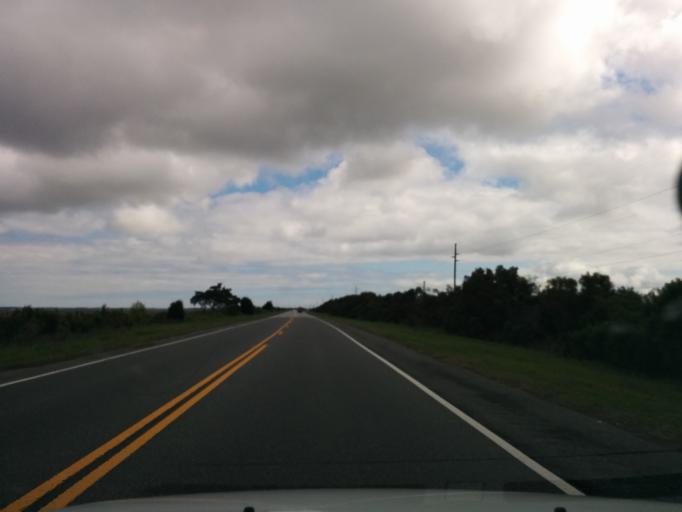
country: US
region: Georgia
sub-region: Glynn County
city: Brunswick
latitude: 31.0866
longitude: -81.4781
